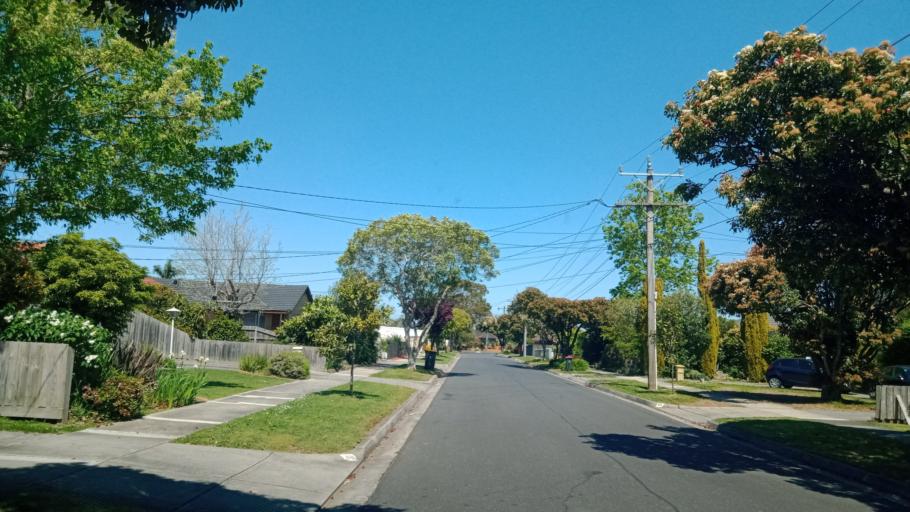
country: AU
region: Victoria
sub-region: Greater Dandenong
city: Springvale
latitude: -37.9283
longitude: 145.1680
